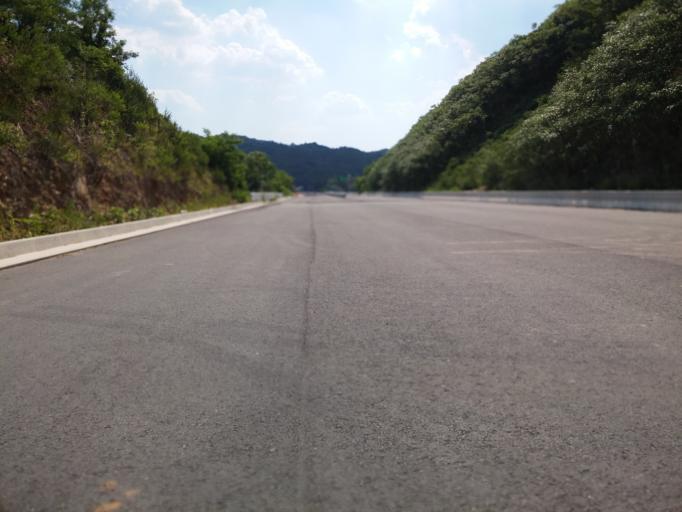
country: KR
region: Daejeon
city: Sintansin
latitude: 36.5040
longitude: 127.4797
